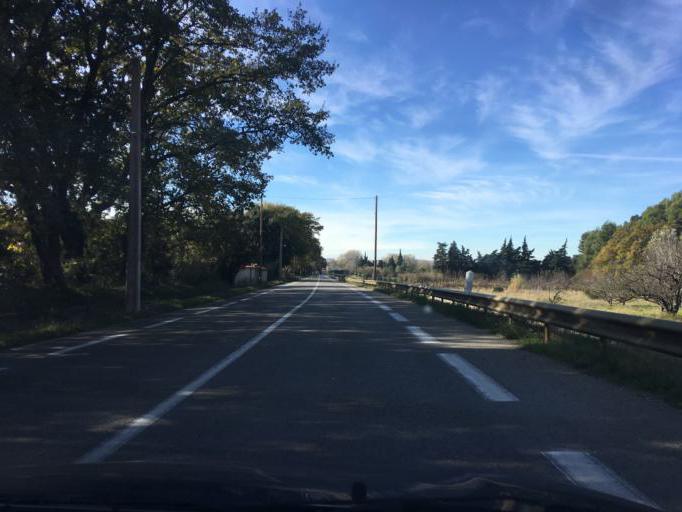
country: FR
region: Provence-Alpes-Cote d'Azur
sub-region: Departement des Bouches-du-Rhone
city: Mallemort
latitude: 43.7566
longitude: 5.1566
